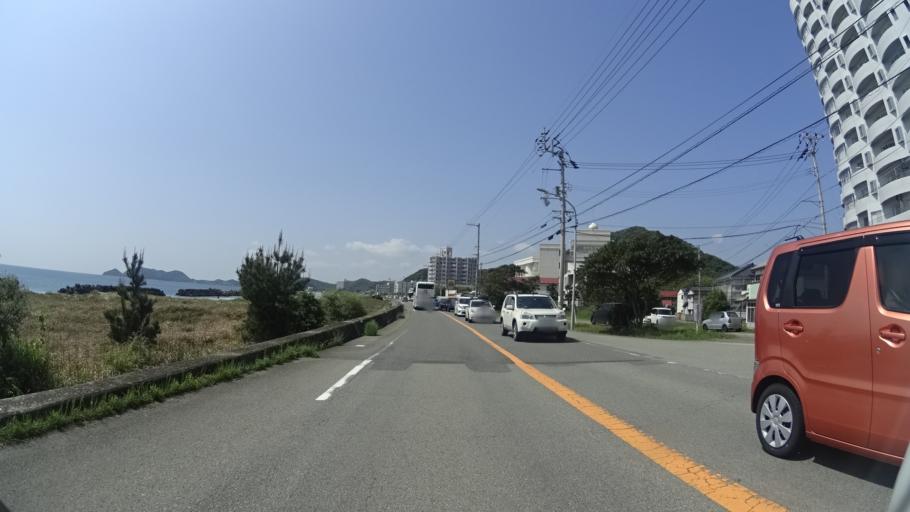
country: JP
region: Tokushima
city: Narutocho-mitsuishi
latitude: 34.2121
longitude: 134.6287
